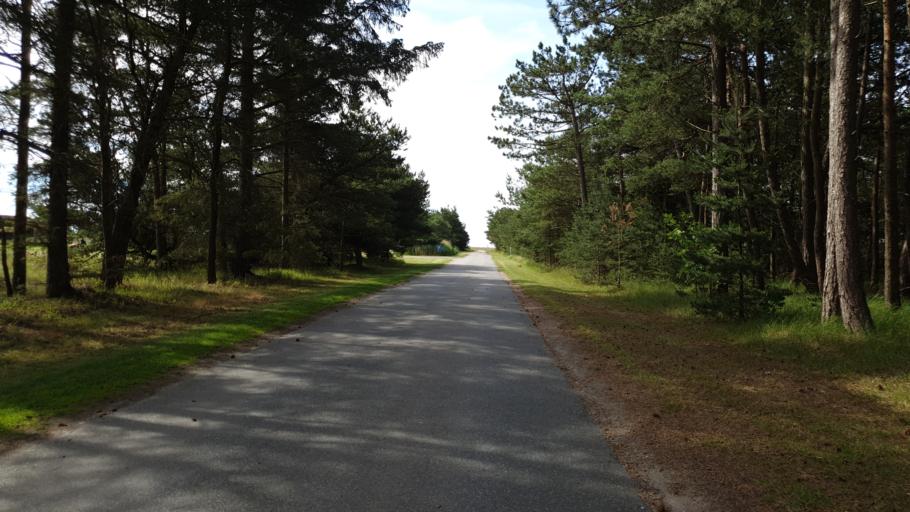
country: DK
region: North Denmark
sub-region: Laeso Kommune
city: Byrum
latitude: 57.2413
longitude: 10.9896
